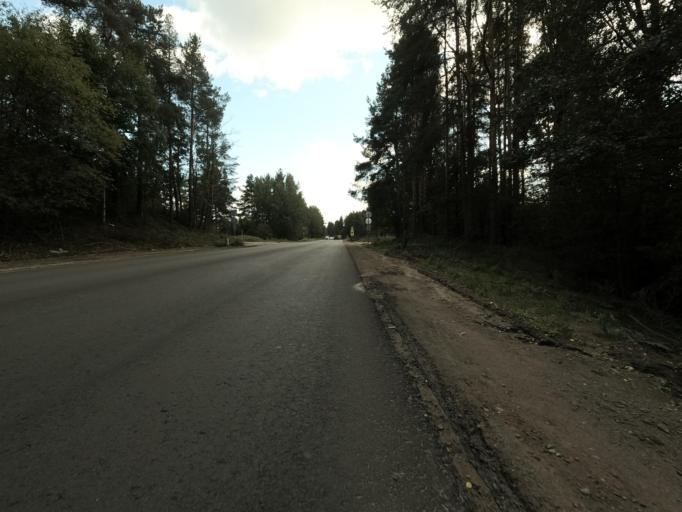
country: RU
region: Leningrad
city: Koltushi
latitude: 59.9637
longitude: 30.6584
